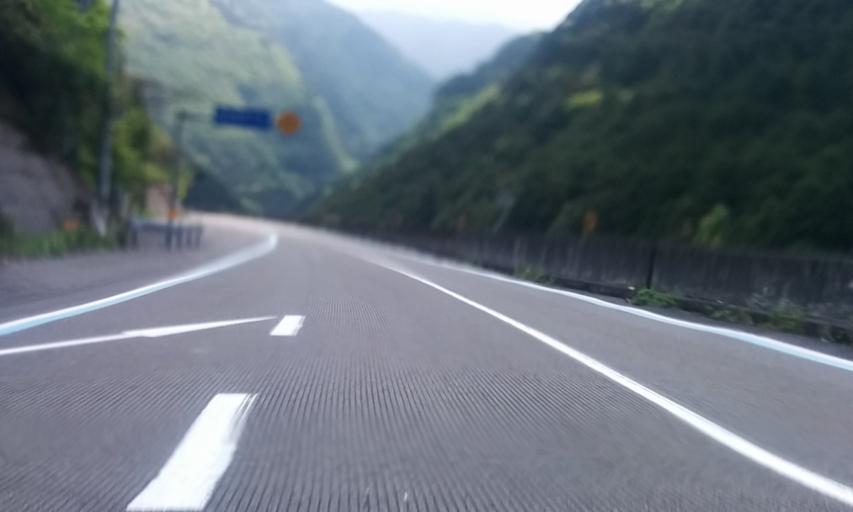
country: JP
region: Ehime
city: Saijo
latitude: 33.8139
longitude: 133.2316
